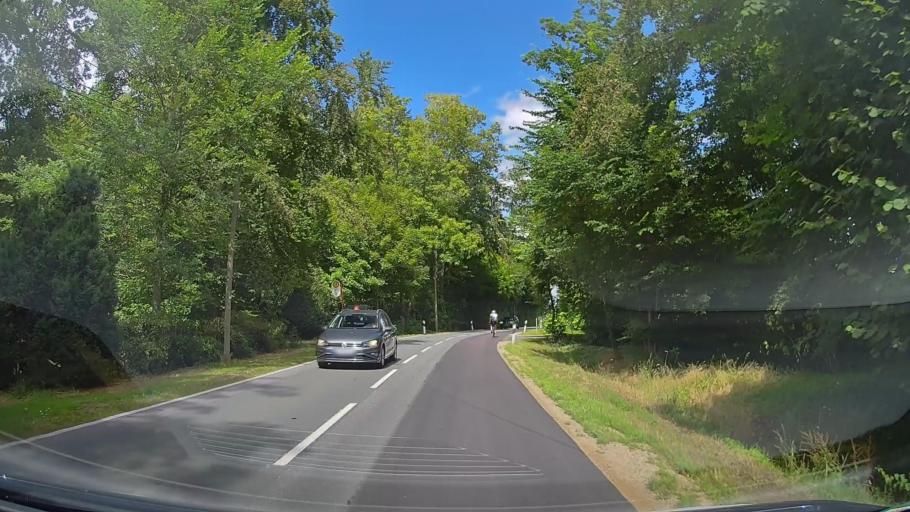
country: DE
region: Lower Saxony
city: Belm
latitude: 52.3709
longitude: 8.1509
